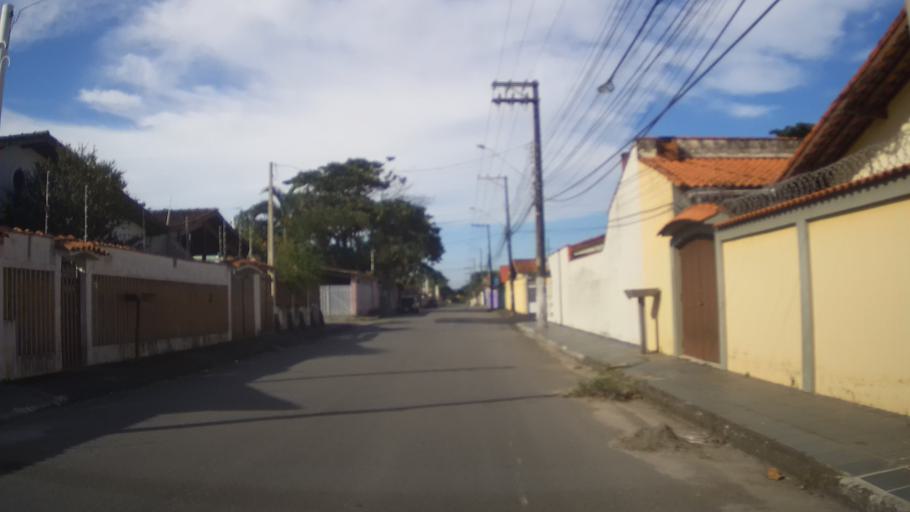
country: BR
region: Sao Paulo
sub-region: Itanhaem
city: Itanhaem
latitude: -24.1630
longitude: -46.7492
